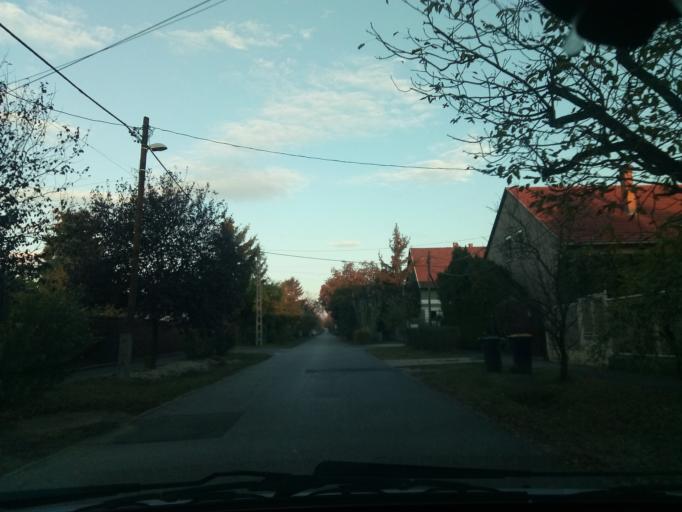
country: HU
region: Budapest
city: Budapest XVIII. keruelet
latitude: 47.4336
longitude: 19.2202
